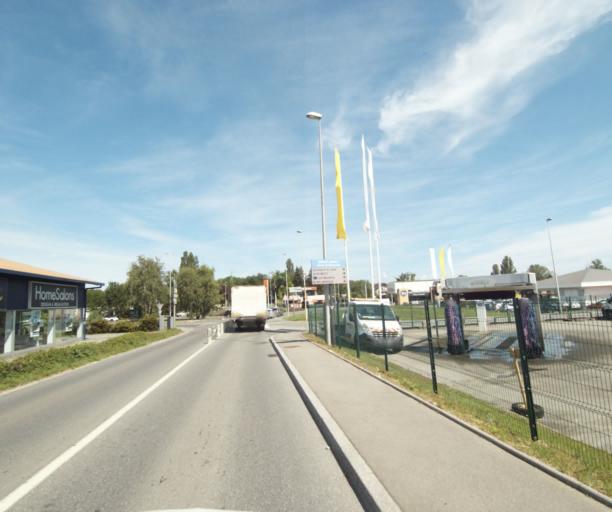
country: FR
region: Rhone-Alpes
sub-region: Departement de la Haute-Savoie
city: Anthy-sur-Leman
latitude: 46.3517
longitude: 6.4401
